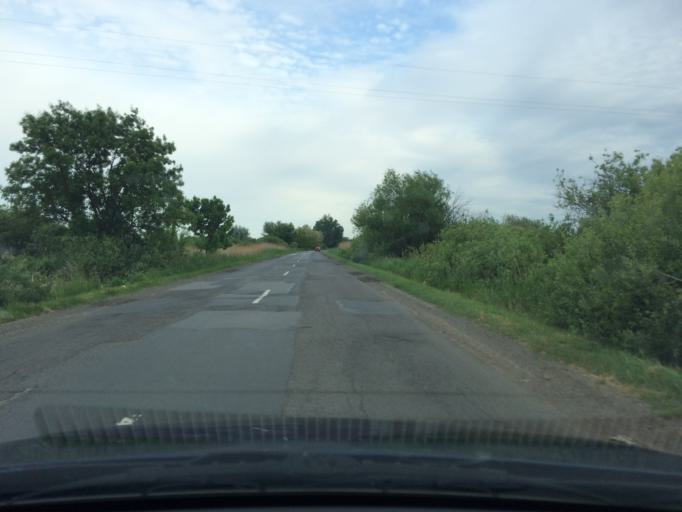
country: HU
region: Hajdu-Bihar
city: Hajdunanas
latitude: 47.8967
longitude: 21.4091
